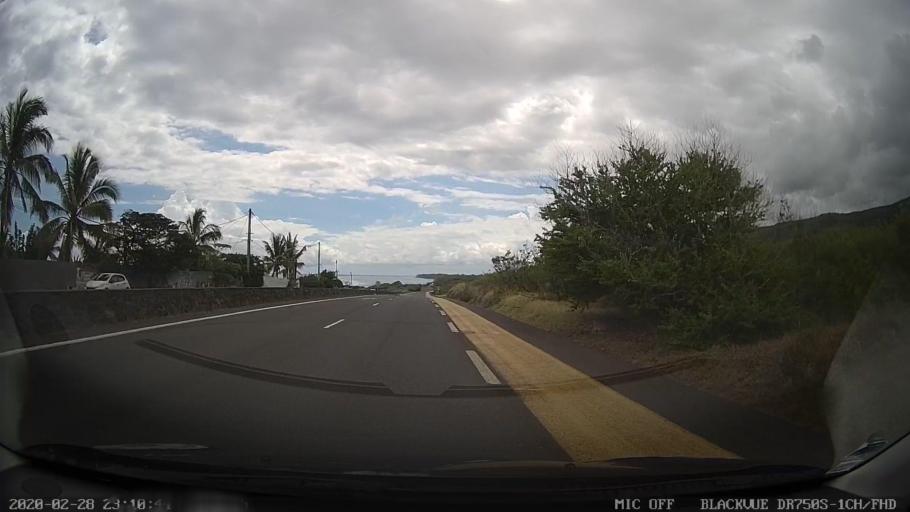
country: RE
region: Reunion
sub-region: Reunion
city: Trois-Bassins
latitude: -21.1159
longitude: 55.2582
